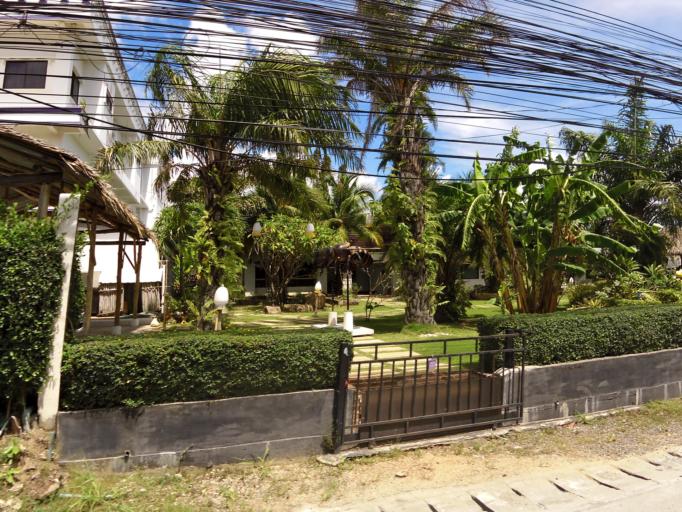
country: TH
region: Phuket
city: Ban Chalong
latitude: 7.8401
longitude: 98.3351
